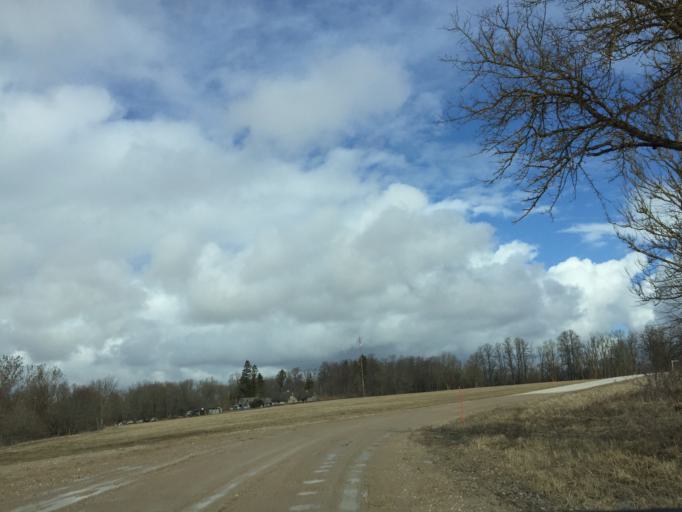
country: EE
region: Laeaene
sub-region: Lihula vald
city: Lihula
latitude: 58.7346
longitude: 23.8278
